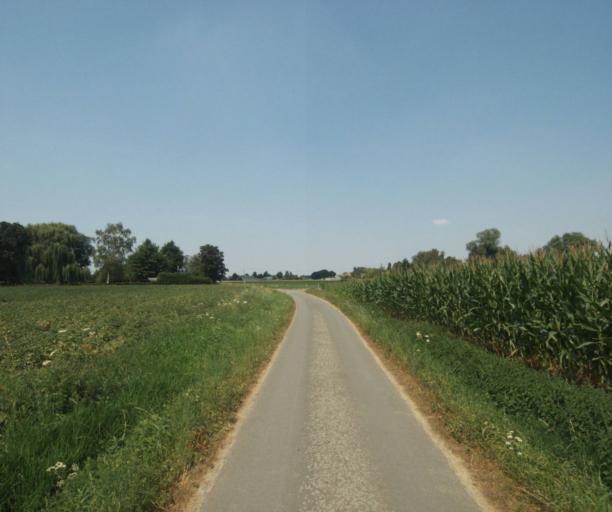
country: FR
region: Nord-Pas-de-Calais
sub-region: Departement du Nord
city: Wambrechies
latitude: 50.7114
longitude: 3.0437
